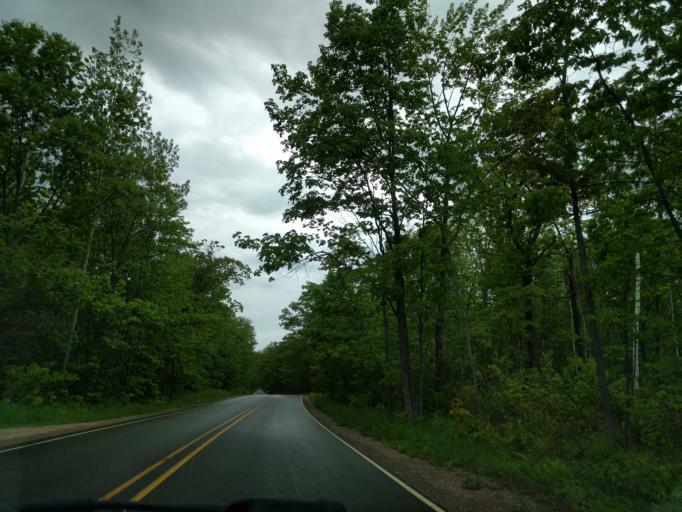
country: US
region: Michigan
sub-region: Marquette County
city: Trowbridge Park
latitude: 46.5674
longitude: -87.4640
